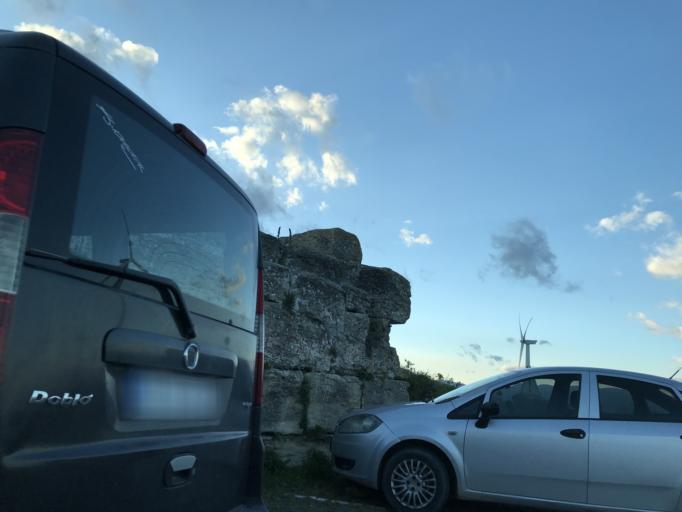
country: TR
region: Hatay
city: Buyukcat
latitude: 36.0920
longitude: 36.0364
